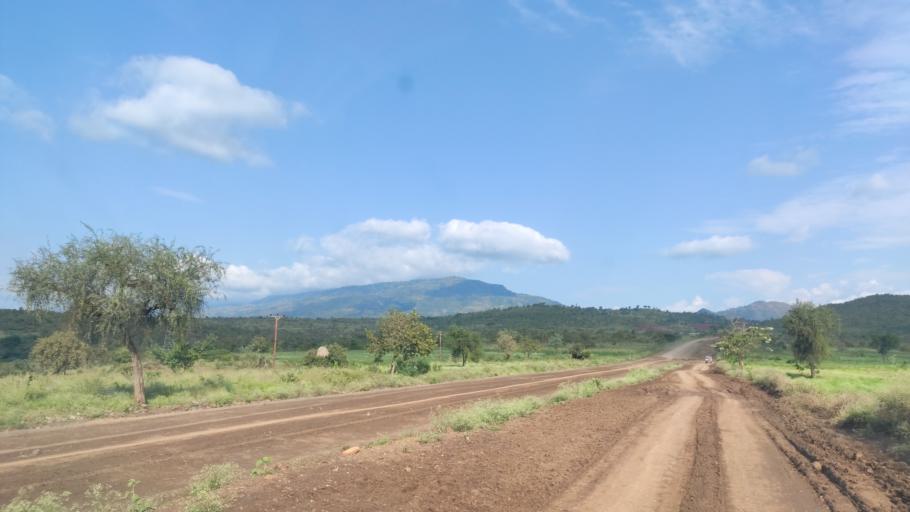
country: ET
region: Southern Nations, Nationalities, and People's Region
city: Felege Neway
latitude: 6.4348
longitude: 37.2825
